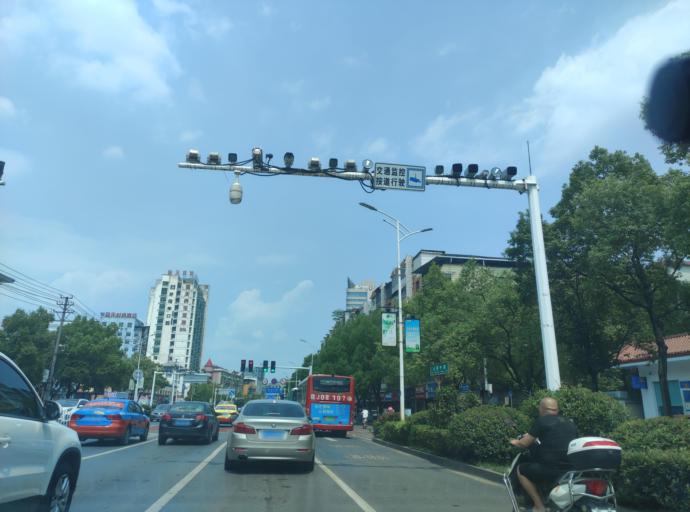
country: CN
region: Jiangxi Sheng
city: Pingxiang
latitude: 27.6407
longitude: 113.8615
